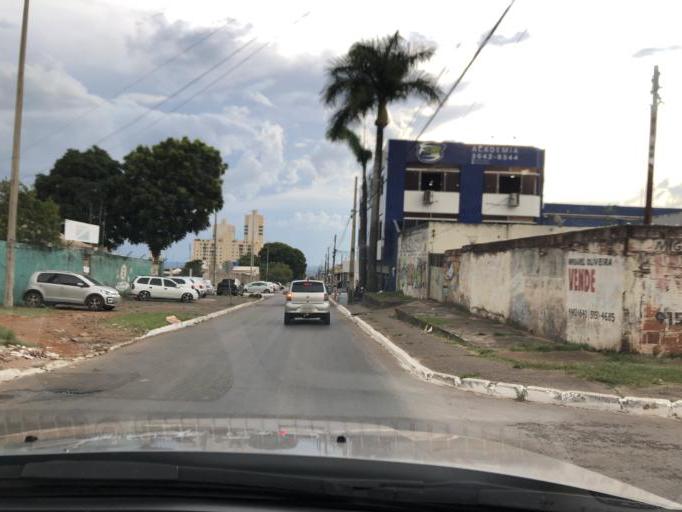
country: BR
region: Federal District
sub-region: Brasilia
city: Brasilia
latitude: -15.8219
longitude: -48.1077
